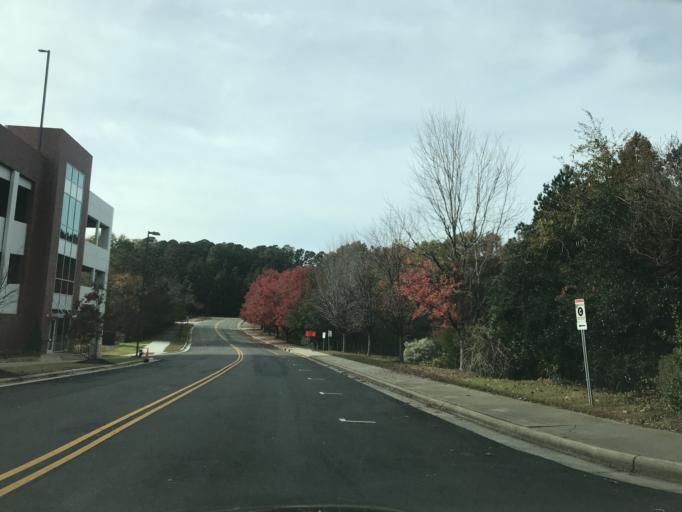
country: US
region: North Carolina
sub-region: Wake County
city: West Raleigh
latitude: 35.7715
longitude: -78.6785
